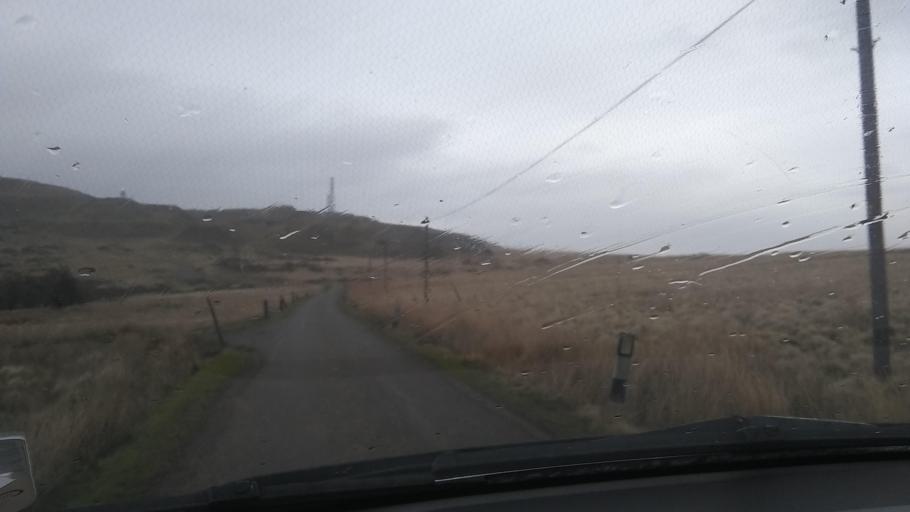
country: GB
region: England
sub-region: Worcestershire
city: Tenbury Wells
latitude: 52.3893
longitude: -2.5967
